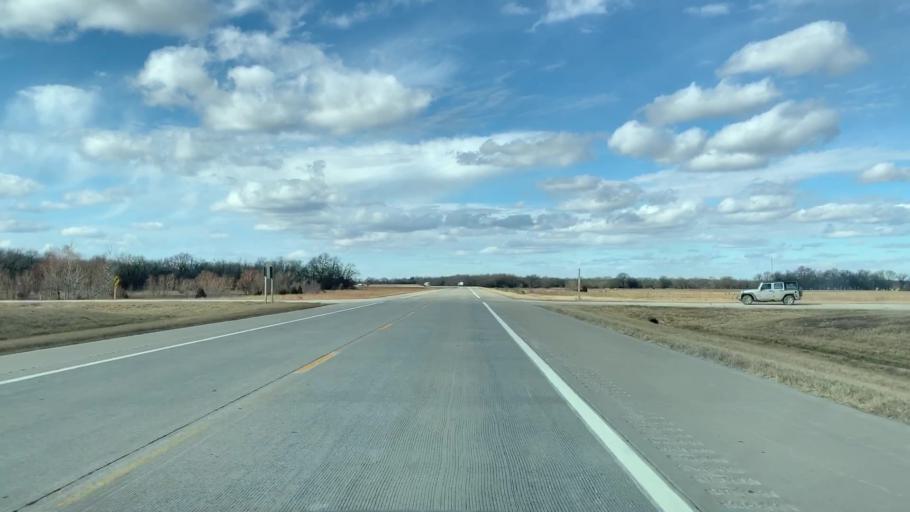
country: US
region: Kansas
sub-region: Labette County
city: Parsons
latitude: 37.3553
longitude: -95.2138
